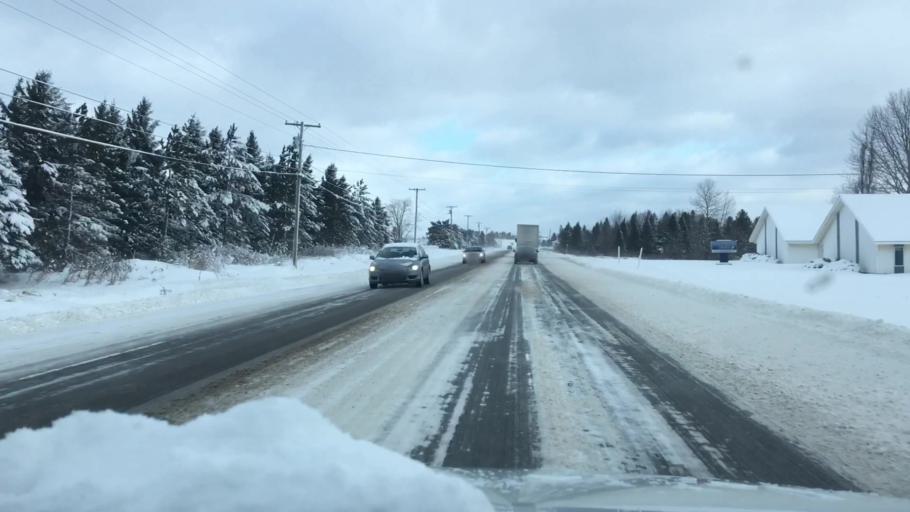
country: US
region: Maine
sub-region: Aroostook County
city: Presque Isle
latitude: 46.7359
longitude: -67.9994
